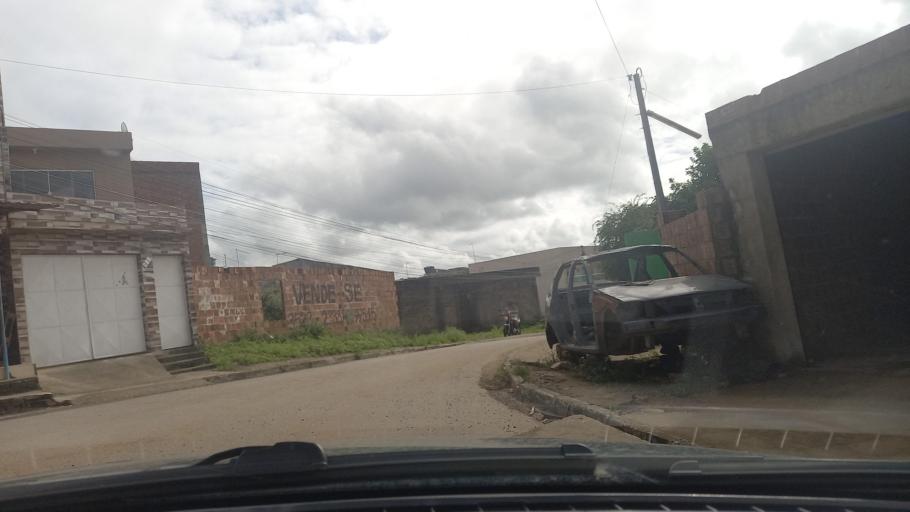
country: BR
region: Pernambuco
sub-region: Vitoria De Santo Antao
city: Vitoria de Santo Antao
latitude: -8.1082
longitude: -35.3061
